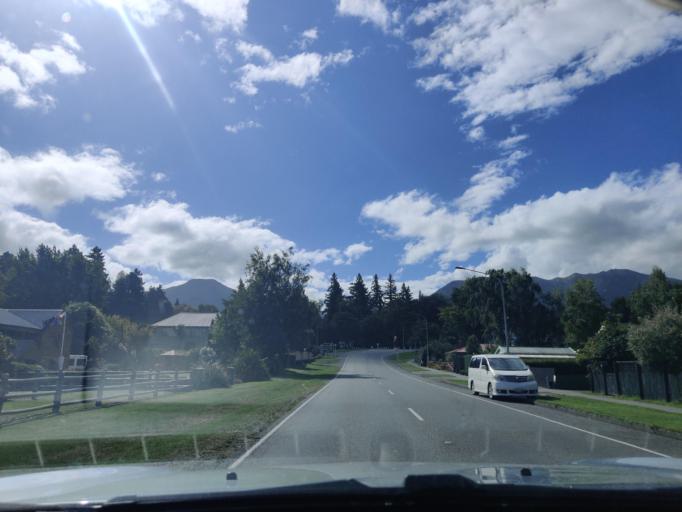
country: NZ
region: Canterbury
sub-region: Hurunui District
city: Amberley
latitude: -42.5271
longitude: 172.8290
